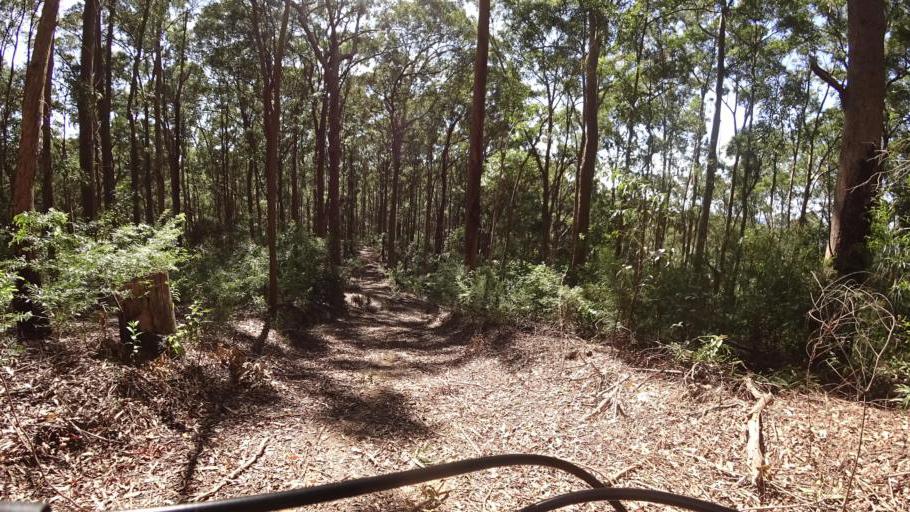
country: AU
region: Queensland
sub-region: Moreton Bay
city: Highvale
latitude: -27.4089
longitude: 152.7789
